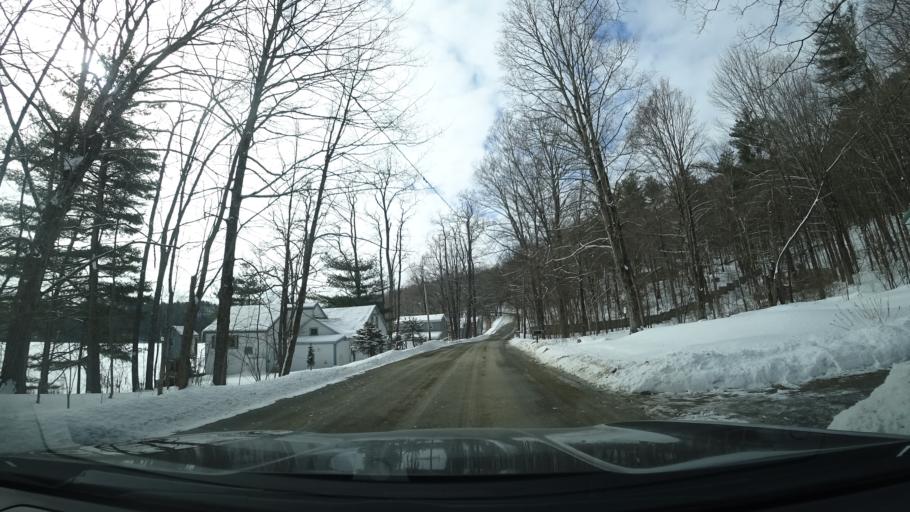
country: US
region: New York
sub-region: Washington County
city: Greenwich
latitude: 43.2164
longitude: -73.3567
